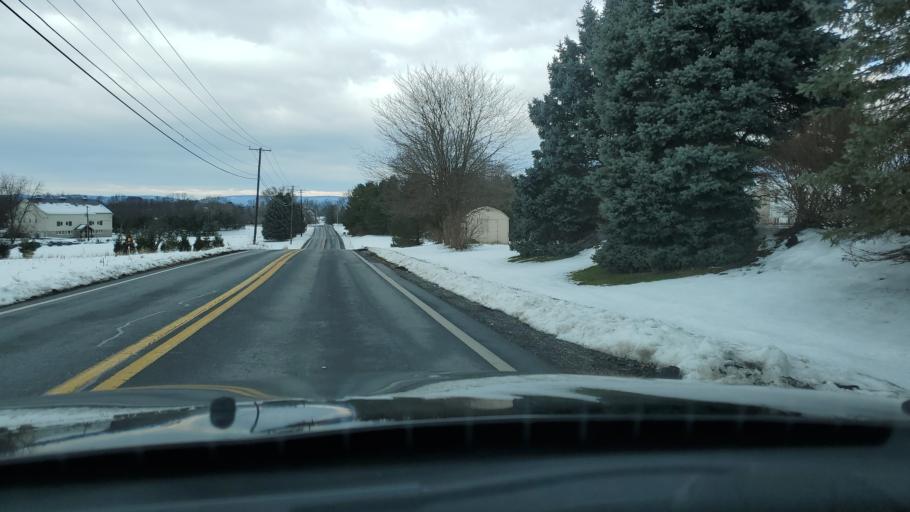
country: US
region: Pennsylvania
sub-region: Cumberland County
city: Mechanicsburg
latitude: 40.2124
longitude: -77.0399
